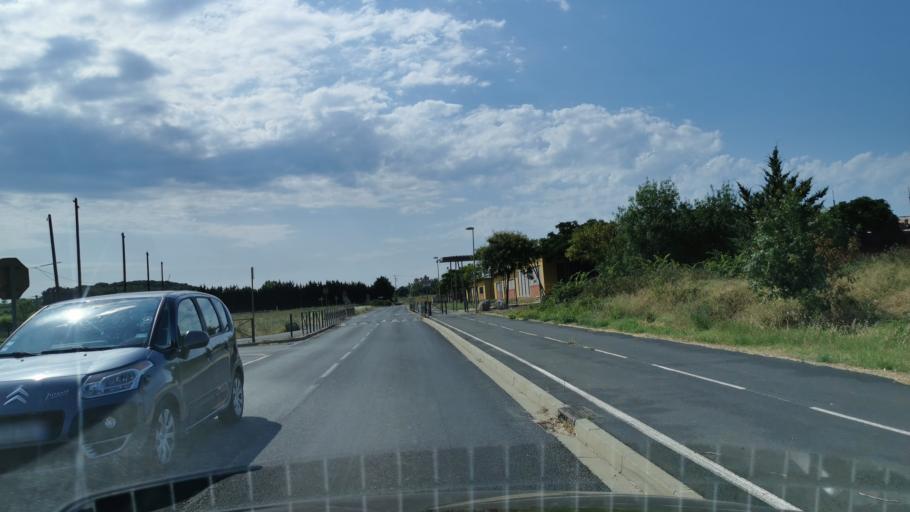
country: FR
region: Languedoc-Roussillon
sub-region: Departement de l'Herault
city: Cazouls-les-Beziers
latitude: 43.3839
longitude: 3.1022
